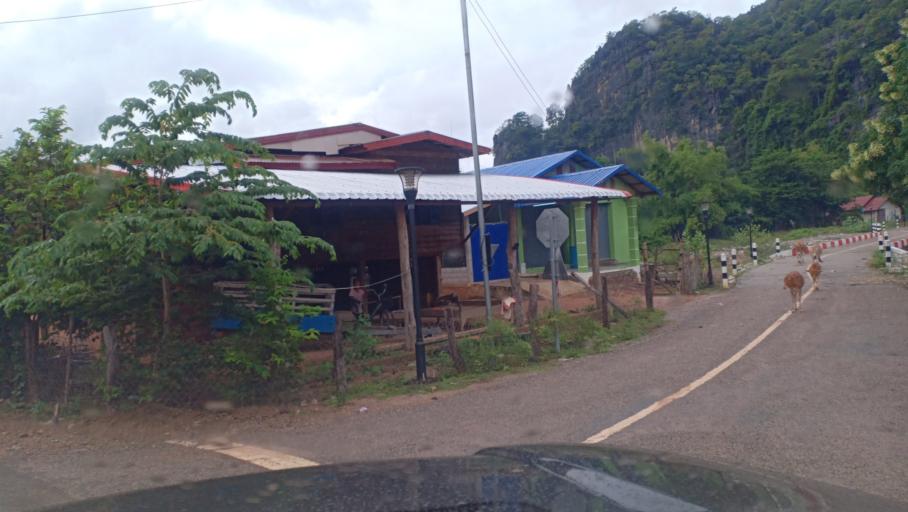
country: LA
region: Khammouan
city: Thakhek
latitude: 17.4285
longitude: 104.8635
